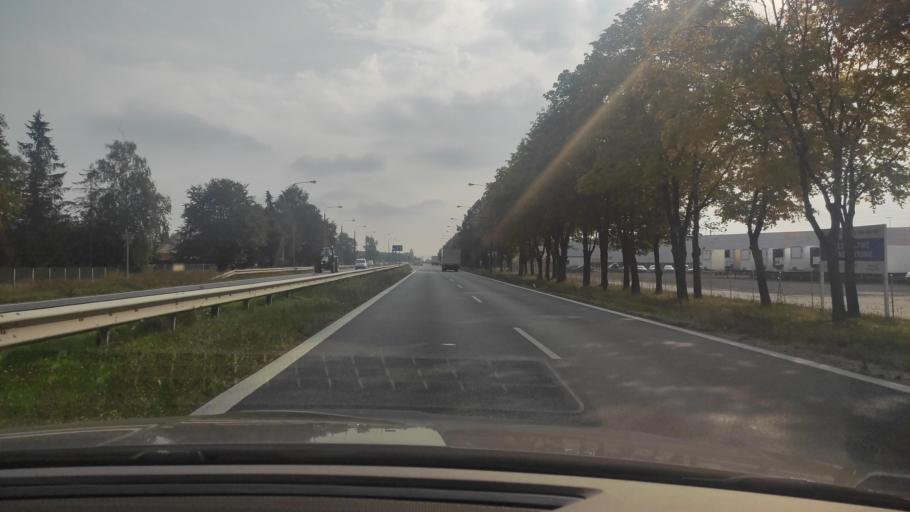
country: PL
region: Greater Poland Voivodeship
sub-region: Powiat poznanski
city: Swarzedz
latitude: 52.4020
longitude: 17.1337
